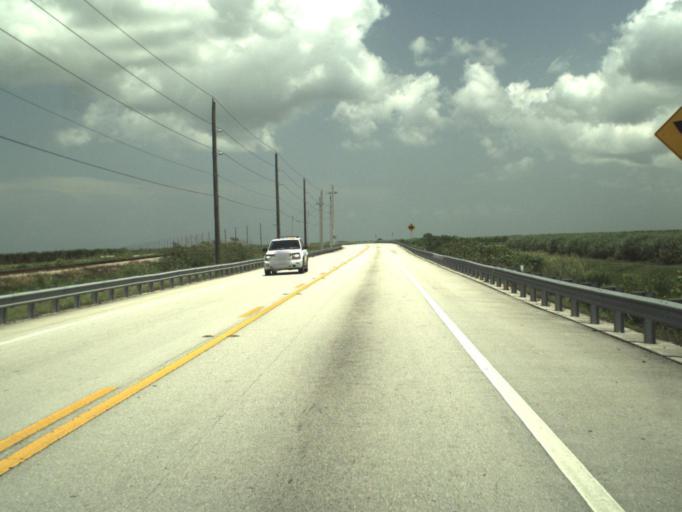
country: US
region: Florida
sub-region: Palm Beach County
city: Belle Glade
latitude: 26.7451
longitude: -80.6606
